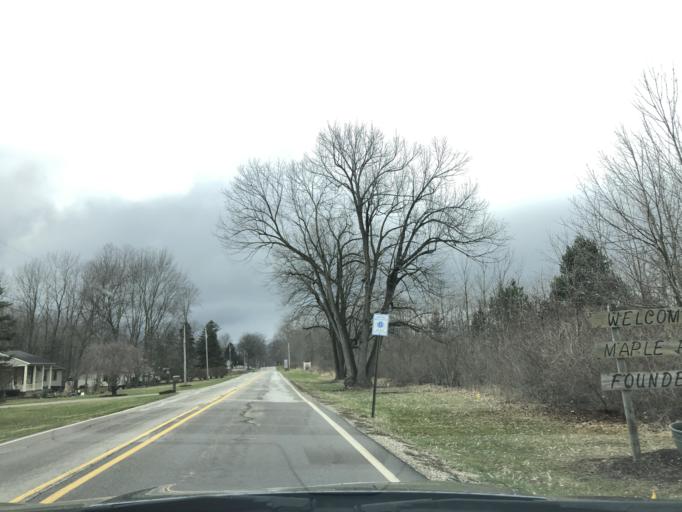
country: US
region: Michigan
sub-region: Clinton County
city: Fowler
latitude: 43.1047
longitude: -84.6801
